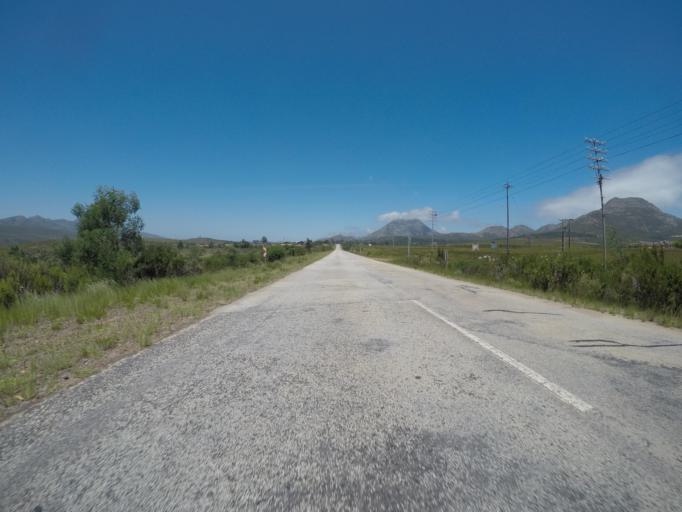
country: ZA
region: Eastern Cape
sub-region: Cacadu District Municipality
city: Kareedouw
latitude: -33.9434
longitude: 24.2698
